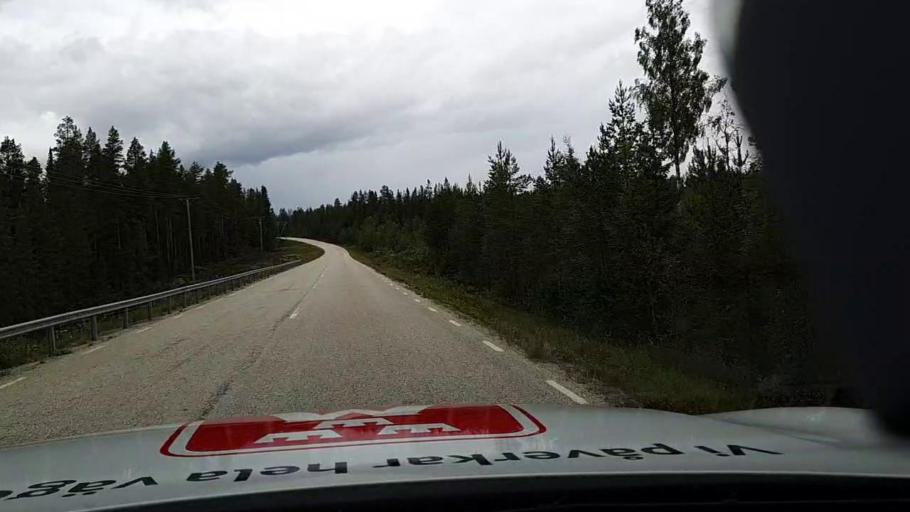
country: SE
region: Jaemtland
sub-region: Are Kommun
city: Jarpen
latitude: 62.7962
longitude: 13.6782
